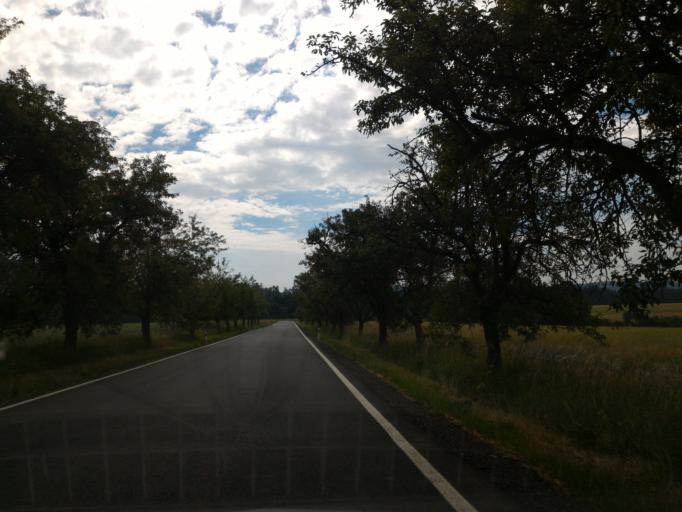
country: CZ
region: Vysocina
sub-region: Okres Jihlava
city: Telc
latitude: 49.1506
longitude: 15.5360
